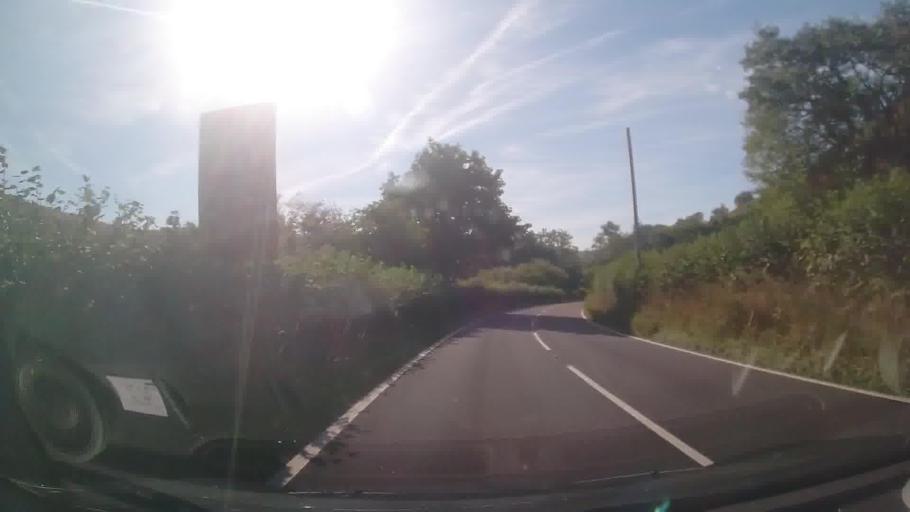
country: GB
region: Wales
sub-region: Sir Powys
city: Hay
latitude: 51.9483
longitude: -3.1908
